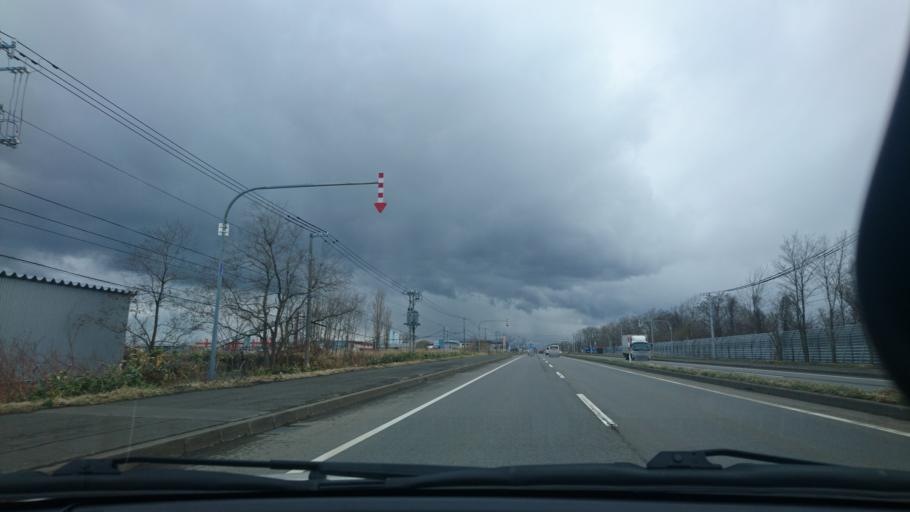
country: JP
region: Hokkaido
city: Ishikari
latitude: 43.2009
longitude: 141.3303
